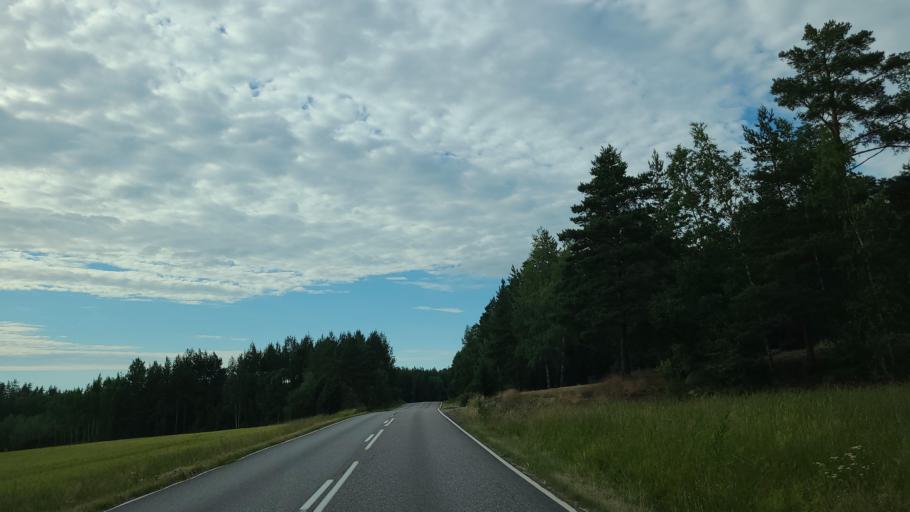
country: FI
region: Varsinais-Suomi
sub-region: Turku
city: Rymaettylae
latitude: 60.3553
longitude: 21.9540
